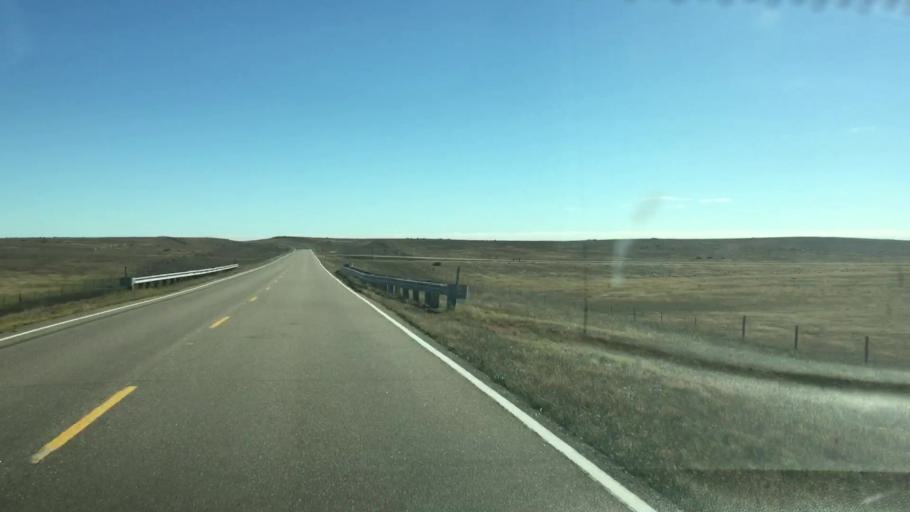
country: US
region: Colorado
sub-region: Lincoln County
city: Limon
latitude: 39.2957
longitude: -103.8649
